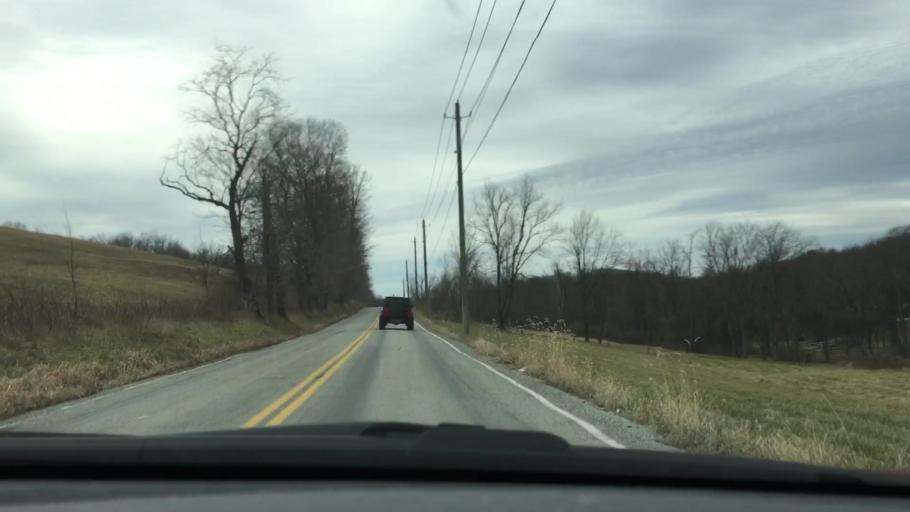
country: US
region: Pennsylvania
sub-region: Washington County
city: Midland
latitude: 40.2753
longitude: -80.2187
